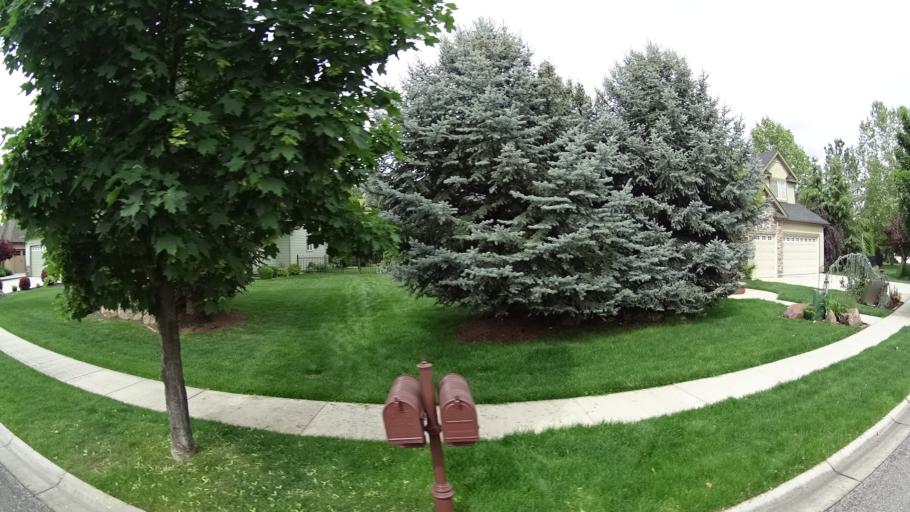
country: US
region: Idaho
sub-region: Ada County
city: Eagle
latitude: 43.6797
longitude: -116.3617
